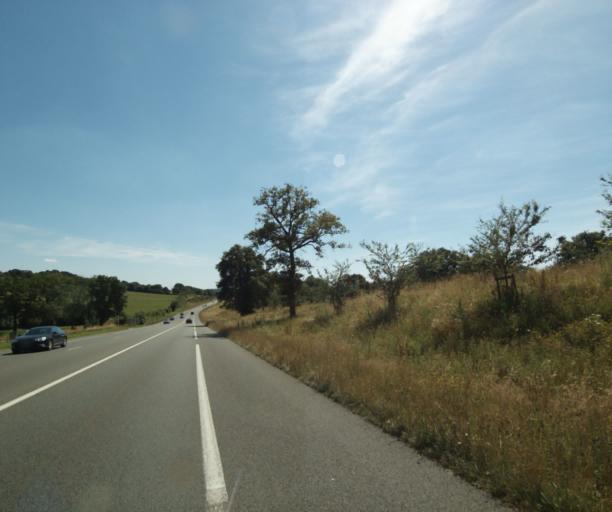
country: FR
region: Pays de la Loire
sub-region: Departement de la Mayenne
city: Montigne-le-Brillant
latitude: 48.0377
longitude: -0.8031
